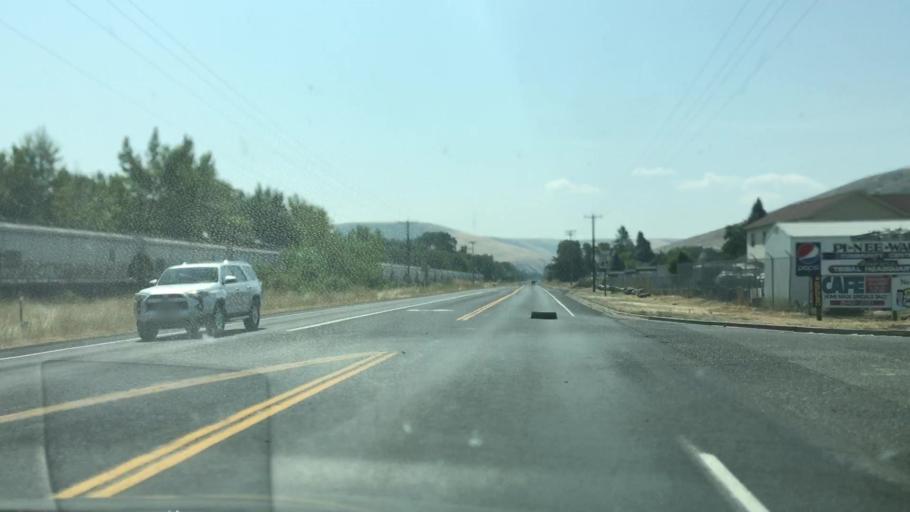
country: US
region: Idaho
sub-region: Nez Perce County
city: Lapwai
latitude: 46.4005
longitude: -116.8009
